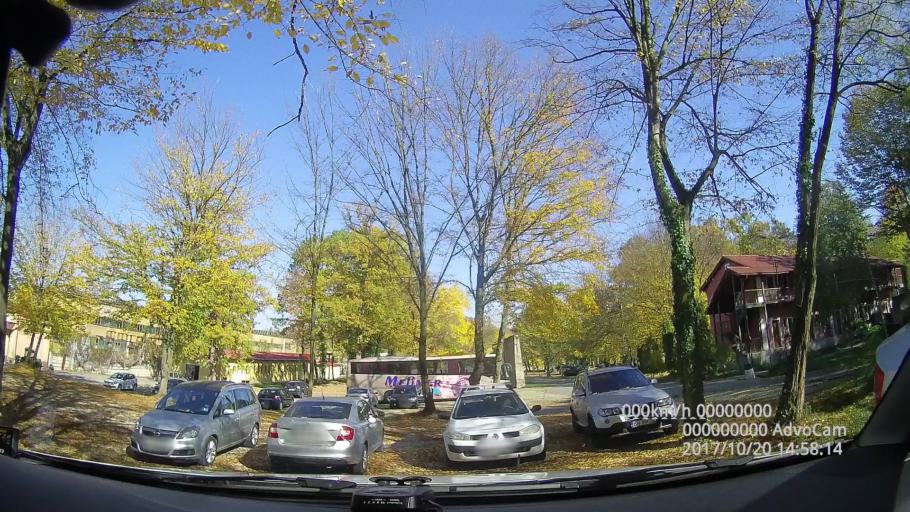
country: RO
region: Hunedoara
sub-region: Comuna Turdas
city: Pricaz
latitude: 45.8409
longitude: 23.1503
